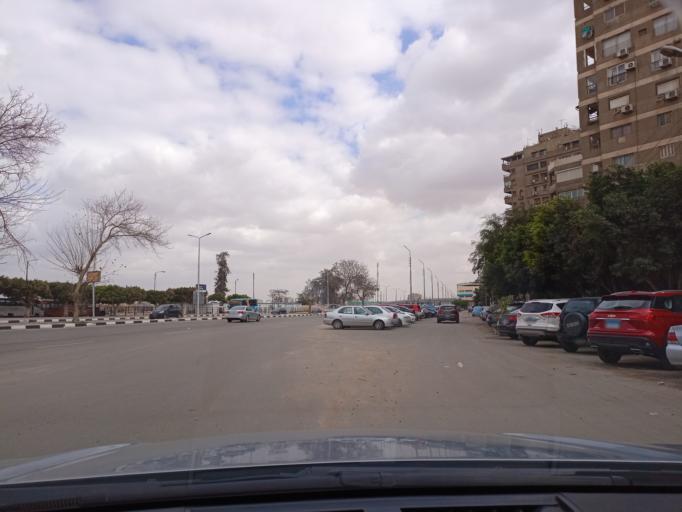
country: EG
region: Muhafazat al Qalyubiyah
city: Al Khankah
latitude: 30.1195
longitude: 31.3515
